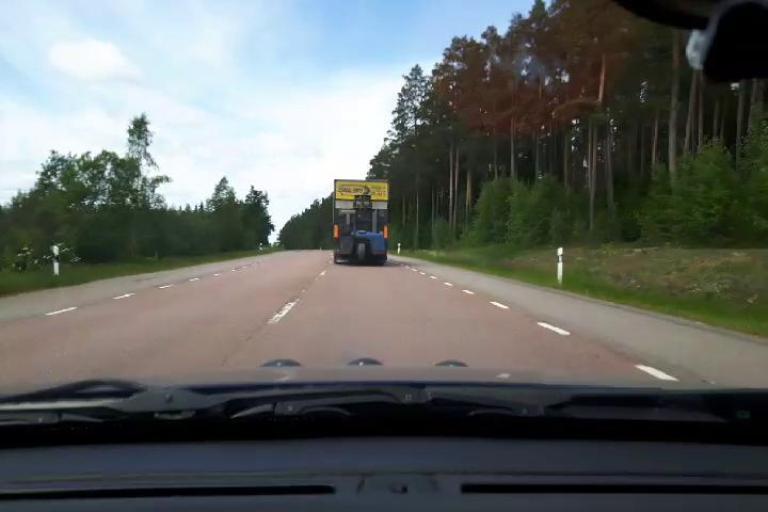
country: SE
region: Uppsala
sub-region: Osthammars Kommun
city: Bjorklinge
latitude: 60.1442
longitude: 17.5018
